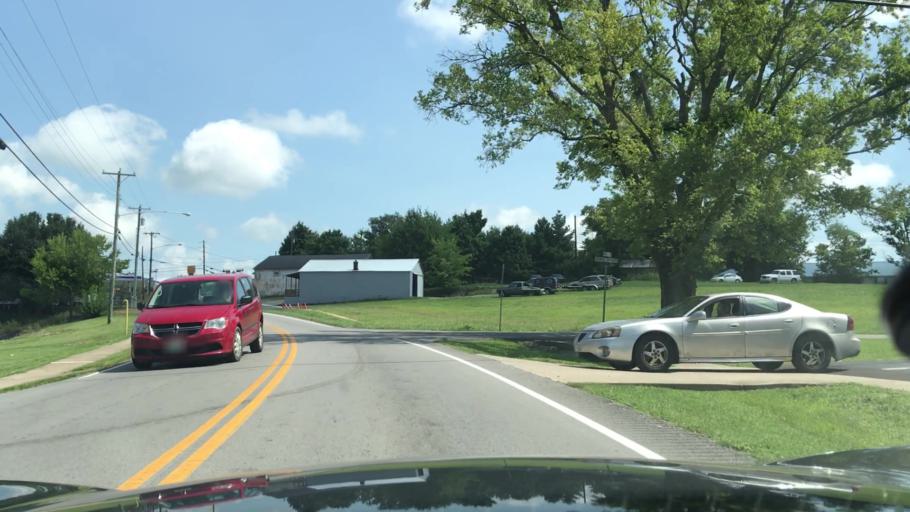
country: US
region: Kentucky
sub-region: Adair County
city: Columbia
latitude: 37.0971
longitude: -85.3144
